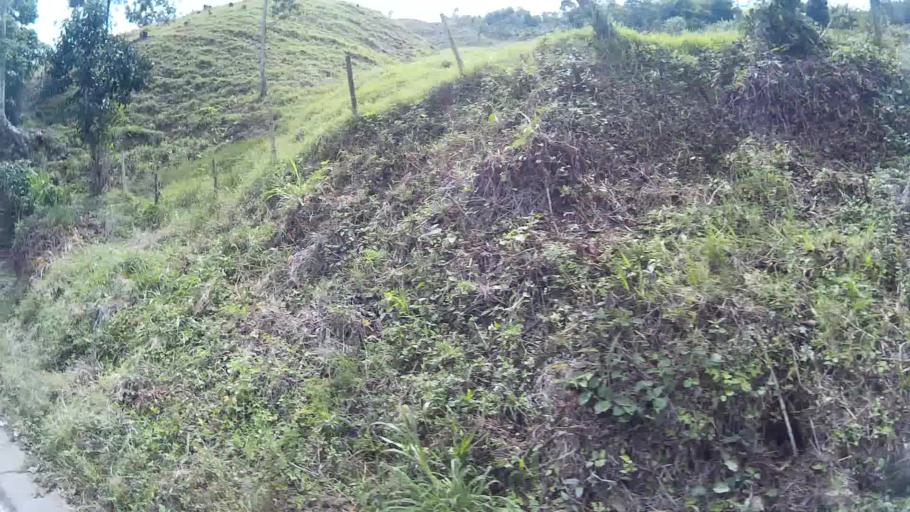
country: CO
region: Risaralda
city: Marsella
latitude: 4.8906
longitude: -75.7459
